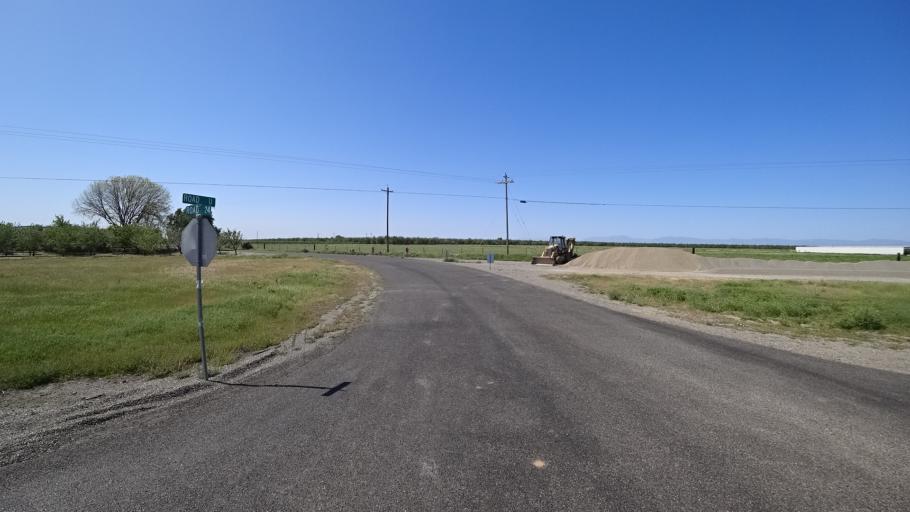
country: US
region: California
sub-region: Glenn County
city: Hamilton City
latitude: 39.7096
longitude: -122.0779
